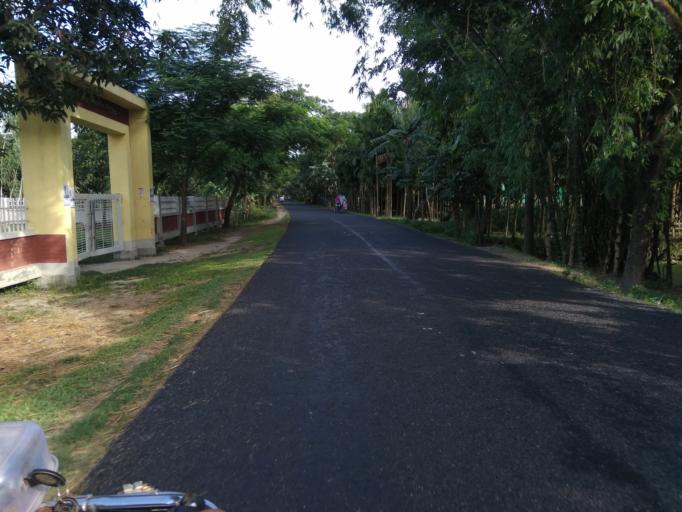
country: BD
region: Rangpur Division
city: Rangpur
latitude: 25.8372
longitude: 89.1144
